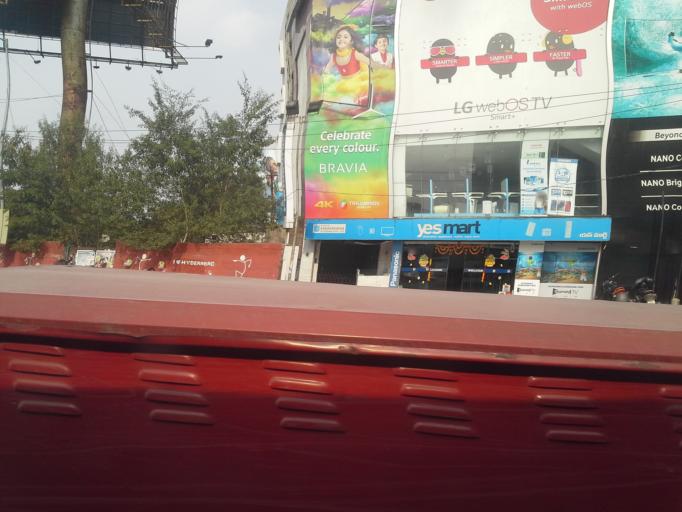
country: IN
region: Telangana
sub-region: Rangareddi
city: Kukatpalli
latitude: 17.4513
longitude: 78.3815
